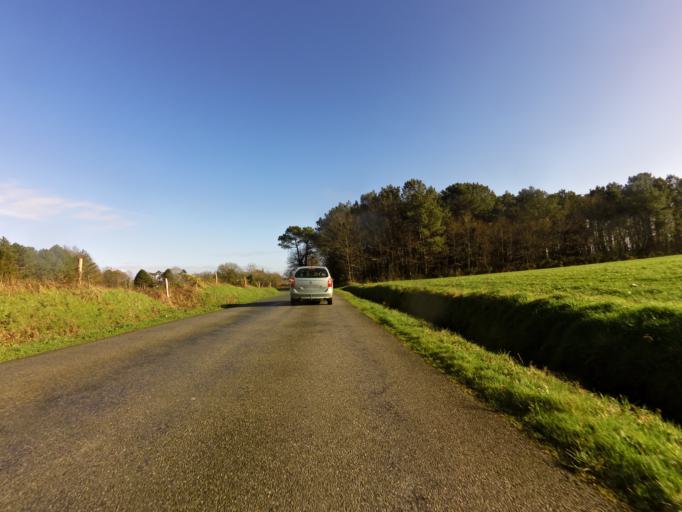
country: FR
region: Brittany
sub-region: Departement du Morbihan
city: Limerzel
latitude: 47.6441
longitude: -2.3681
